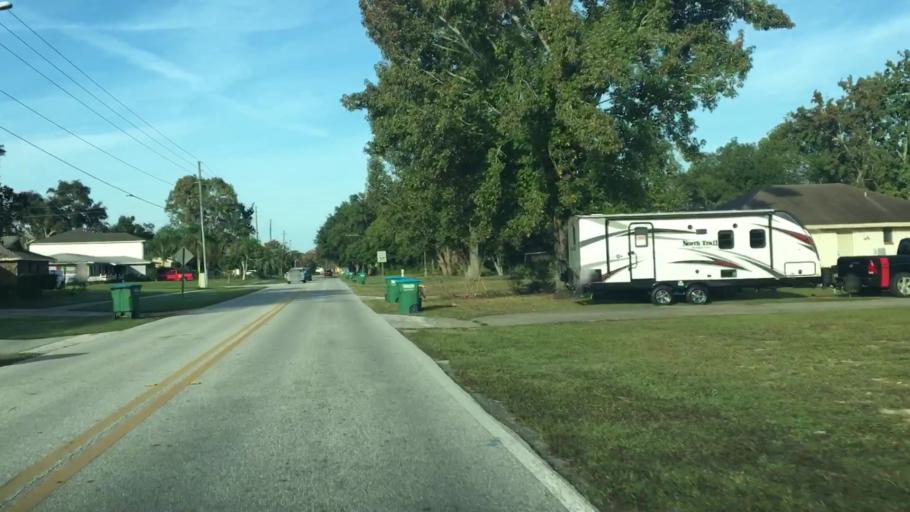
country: US
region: Florida
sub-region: Volusia County
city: Deltona
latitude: 28.9226
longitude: -81.2408
